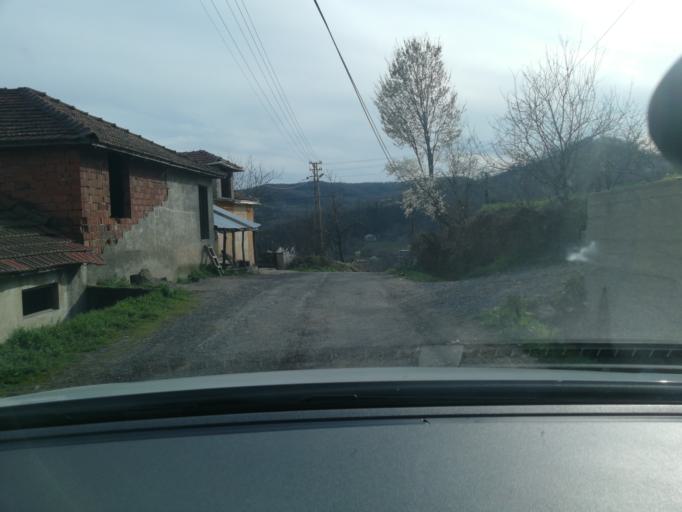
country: TR
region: Zonguldak
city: Kozlu
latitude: 41.3548
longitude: 31.6445
